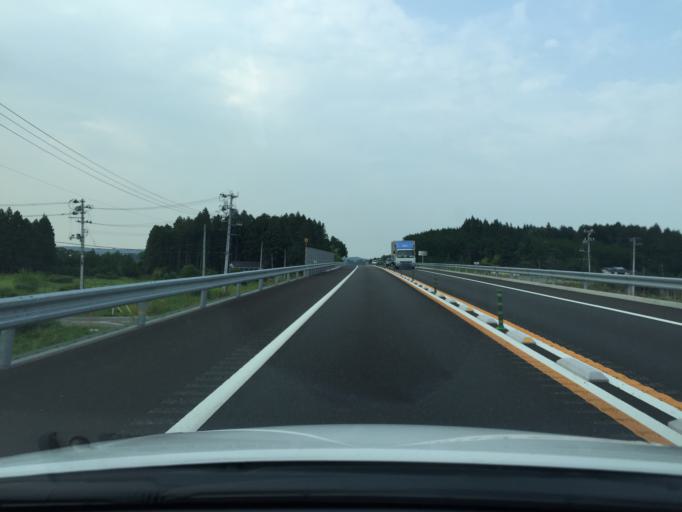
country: JP
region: Fukushima
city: Namie
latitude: 37.5487
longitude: 140.9437
